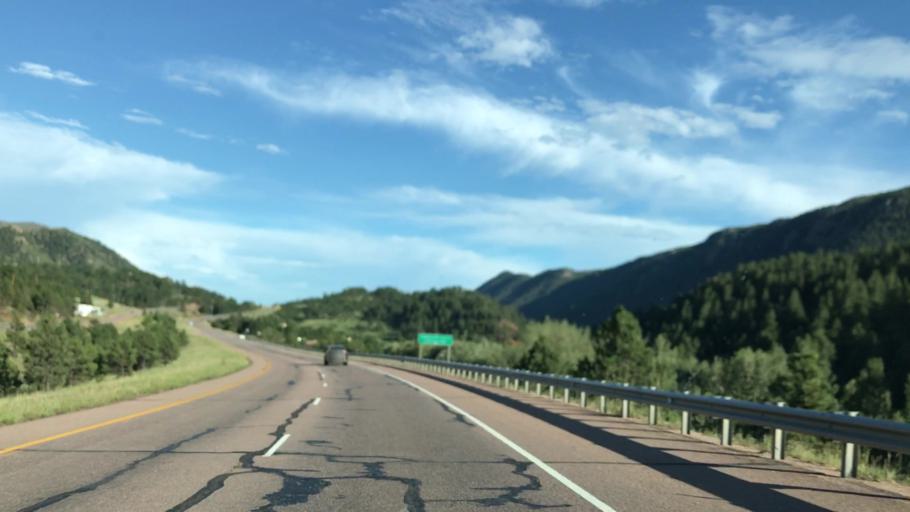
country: US
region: Colorado
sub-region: El Paso County
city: Cascade-Chipita Park
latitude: 38.9440
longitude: -105.0199
